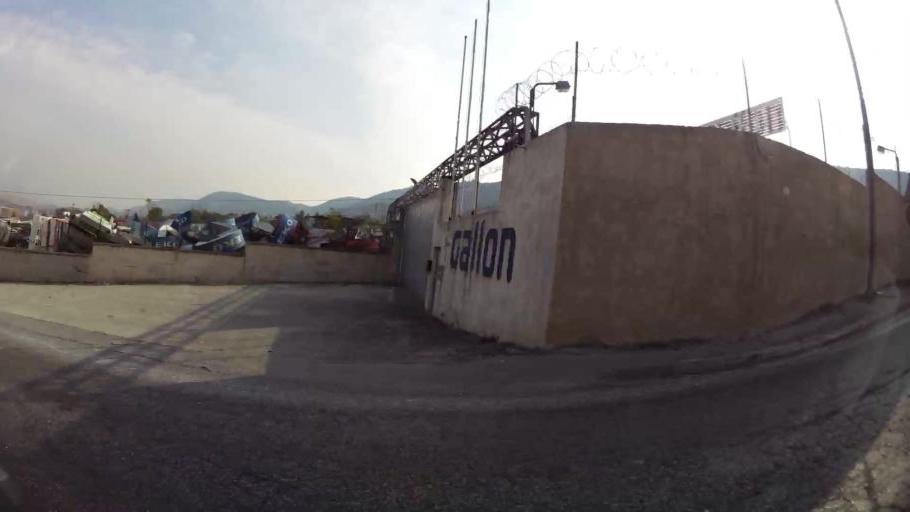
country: GR
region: Attica
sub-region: Nomarchia Athinas
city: Skaramangas
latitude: 38.0278
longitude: 23.6115
